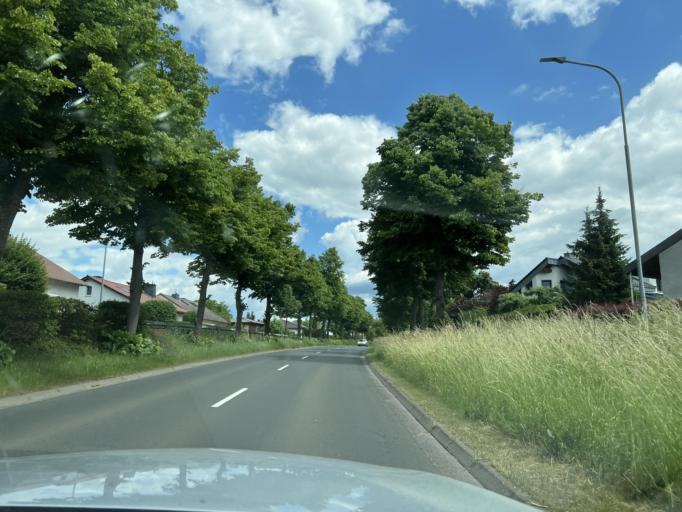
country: DE
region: Hesse
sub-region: Regierungsbezirk Giessen
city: Kirchhain
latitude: 50.8304
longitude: 8.9278
